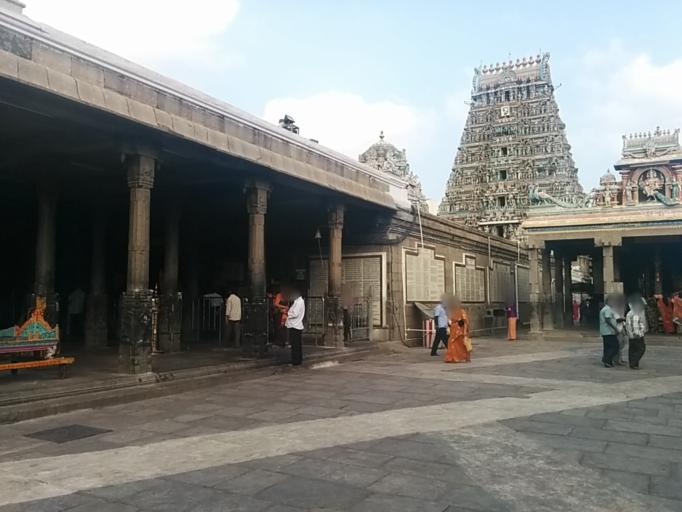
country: IN
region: Tamil Nadu
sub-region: Chennai
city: Gandhi Nagar
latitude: 13.0336
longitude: 80.2695
